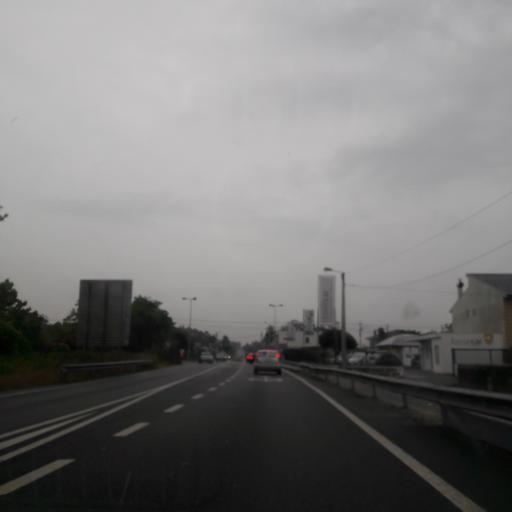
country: PT
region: Porto
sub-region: Vila do Conde
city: Arvore
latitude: 41.3174
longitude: -8.7106
